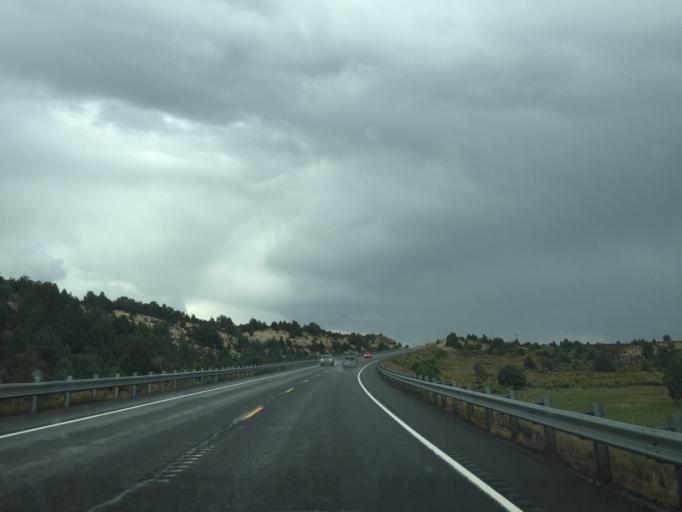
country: US
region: Utah
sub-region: Garfield County
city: Panguitch
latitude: 37.5884
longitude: -112.4753
